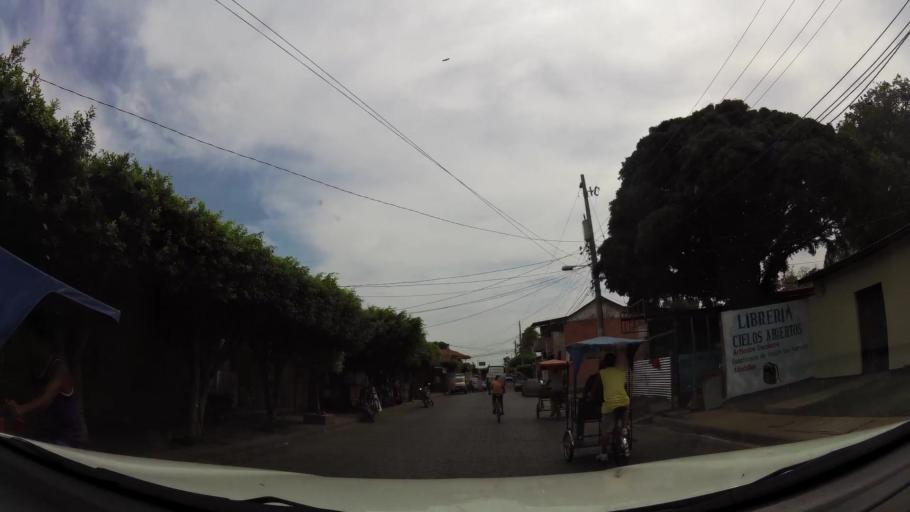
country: NI
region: Rivas
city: Rivas
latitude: 11.4421
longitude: -85.8297
